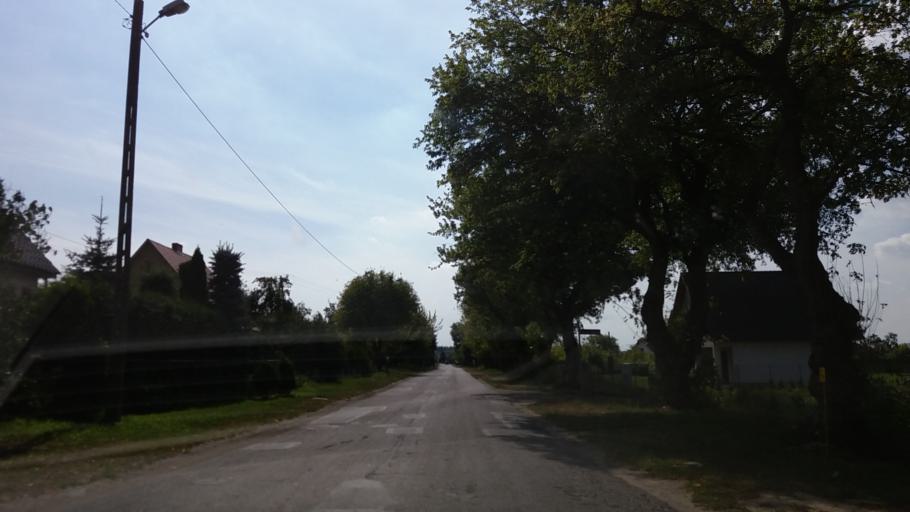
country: PL
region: West Pomeranian Voivodeship
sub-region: Powiat stargardzki
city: Stargard Szczecinski
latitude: 53.3661
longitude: 14.9726
